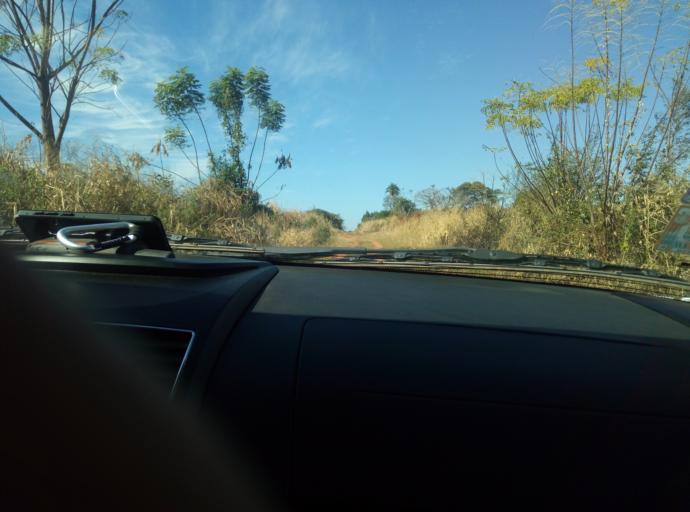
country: PY
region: Caaguazu
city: Carayao
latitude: -25.1757
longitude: -56.3071
